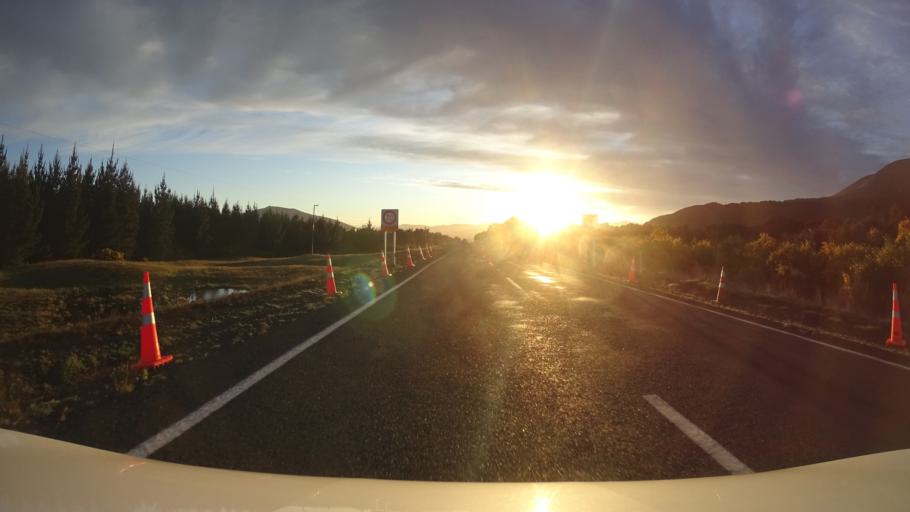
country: NZ
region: Waikato
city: Turangi
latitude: -39.0651
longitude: 175.6643
